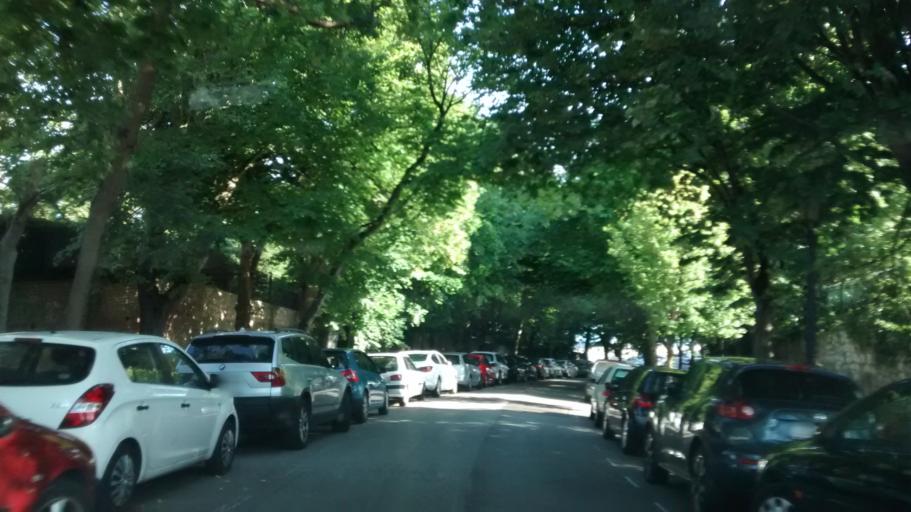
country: ES
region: Cantabria
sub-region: Provincia de Cantabria
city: Santander
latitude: 43.4673
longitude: -3.7796
